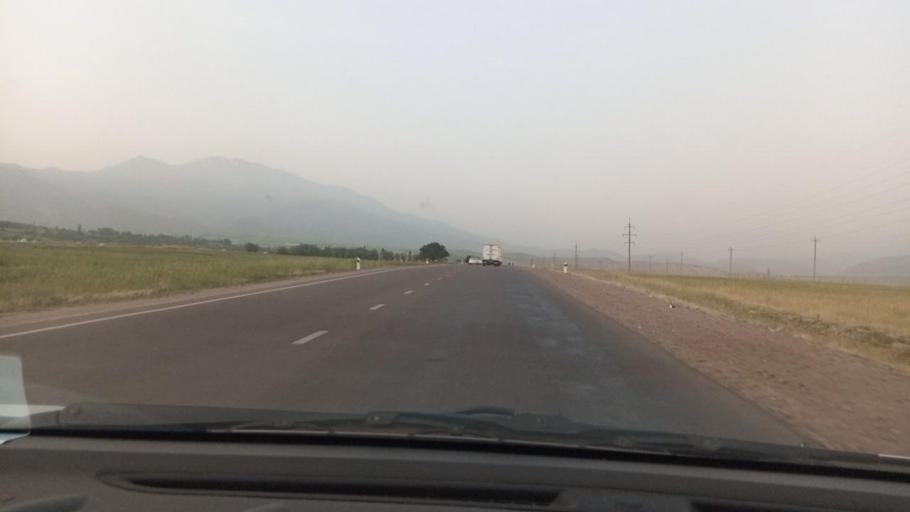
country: UZ
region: Toshkent
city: Angren
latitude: 41.0355
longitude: 70.1441
